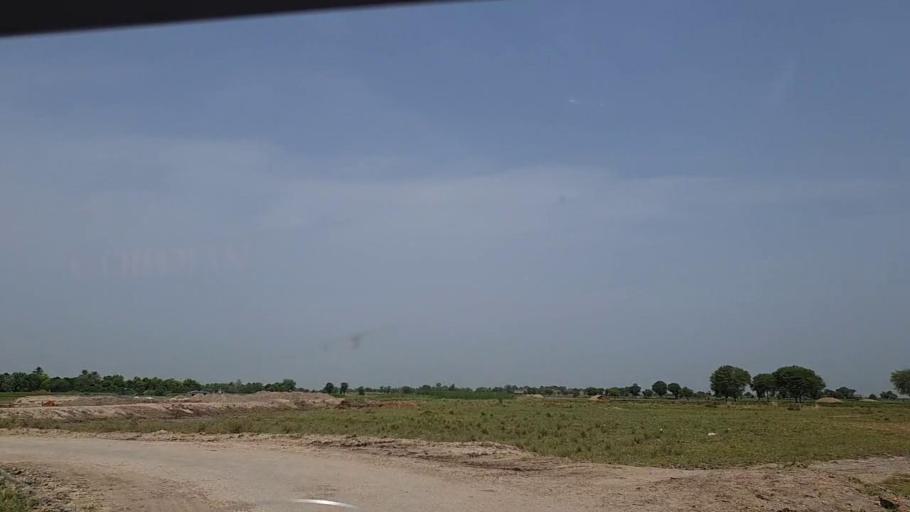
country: PK
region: Sindh
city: Tharu Shah
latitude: 26.9166
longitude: 68.0561
